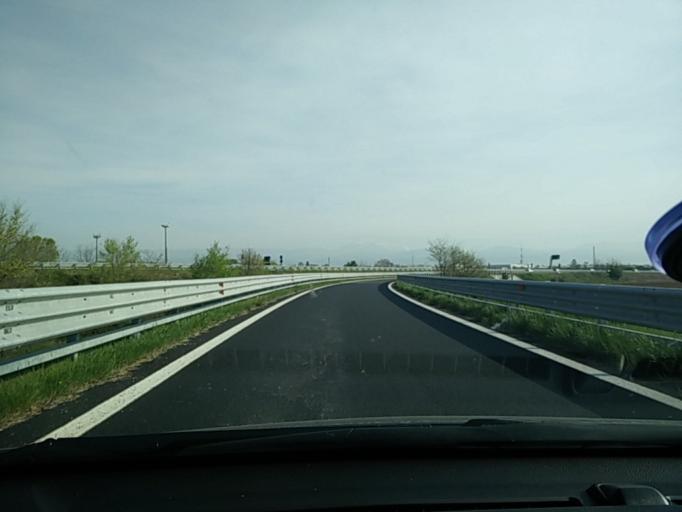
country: IT
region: Friuli Venezia Giulia
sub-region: Provincia di Udine
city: Zugliano-Terenzano-Cargnacco
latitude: 46.0157
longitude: 13.2276
